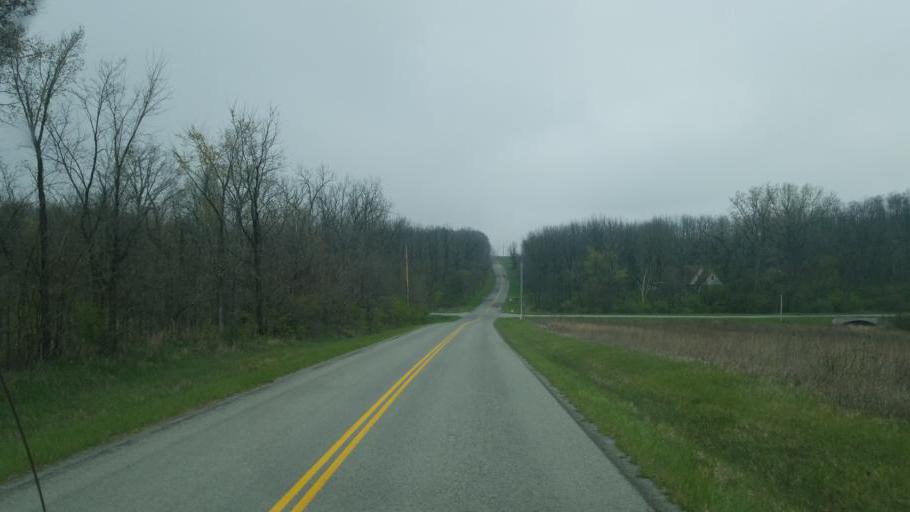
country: US
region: Ohio
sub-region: Logan County
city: Northwood
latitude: 40.4951
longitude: -83.6759
